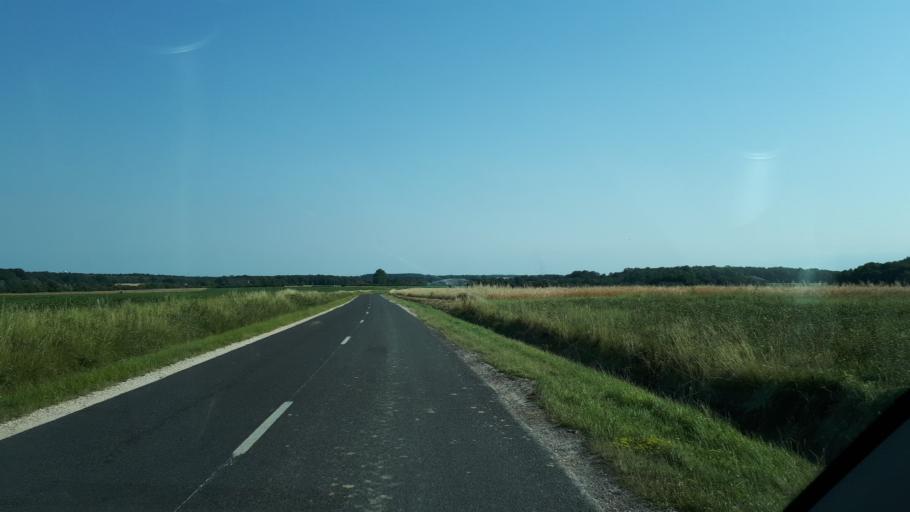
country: FR
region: Centre
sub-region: Departement du Loir-et-Cher
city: La Ville-aux-Clercs
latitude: 47.9491
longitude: 1.0805
